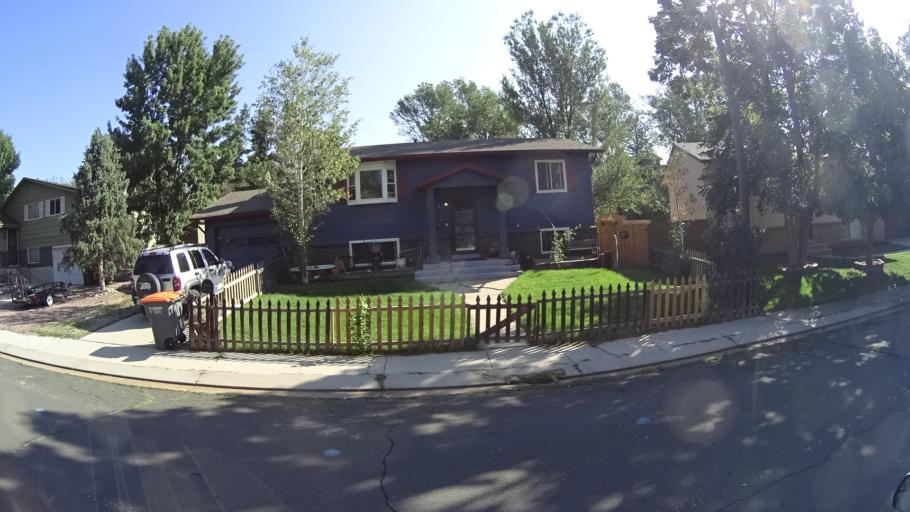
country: US
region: Colorado
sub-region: El Paso County
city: Colorado Springs
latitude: 38.8869
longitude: -104.8387
